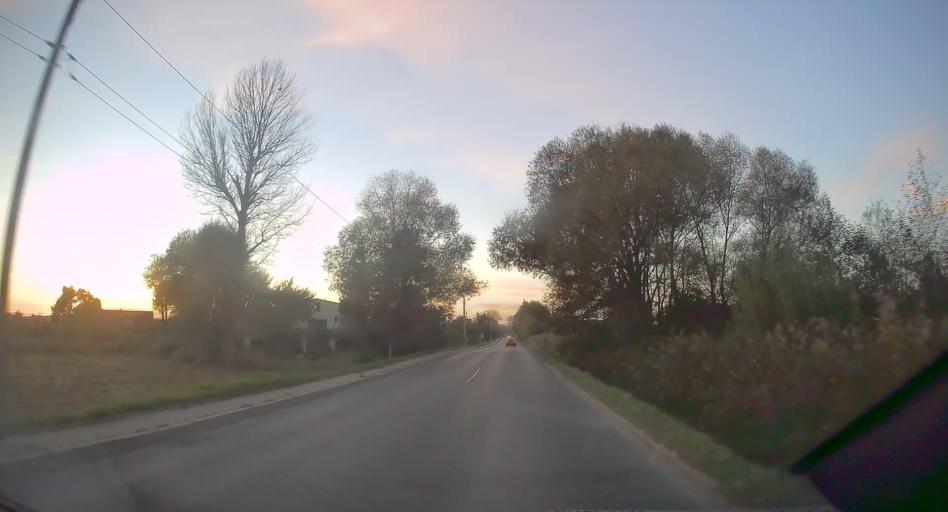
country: PL
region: Lesser Poland Voivodeship
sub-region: Powiat krakowski
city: Rzaska
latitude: 50.1118
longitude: 19.8386
